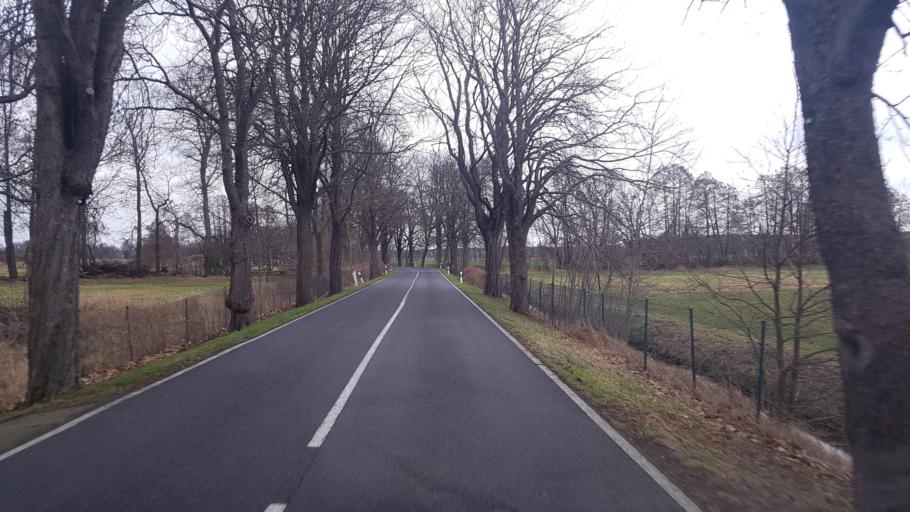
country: DE
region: Brandenburg
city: Drahnsdorf
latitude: 51.9245
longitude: 13.6182
